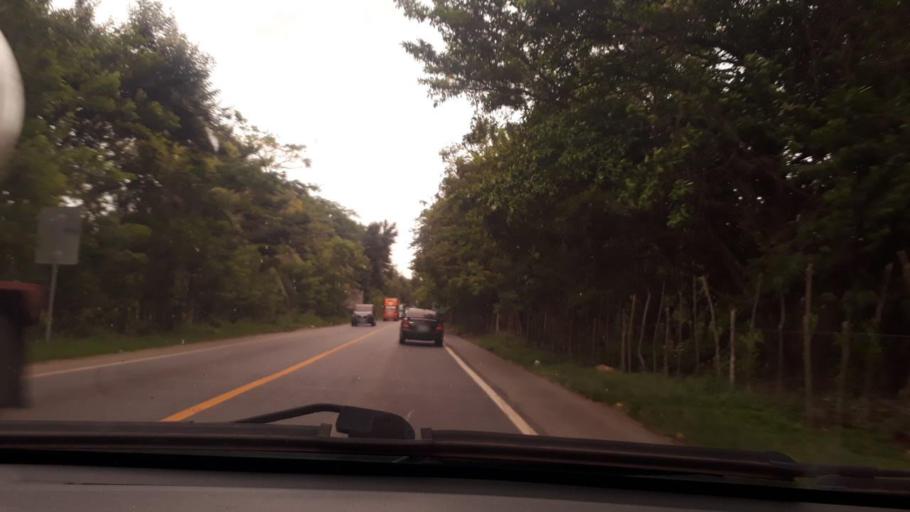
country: GT
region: Izabal
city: Morales
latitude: 15.4990
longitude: -88.8533
